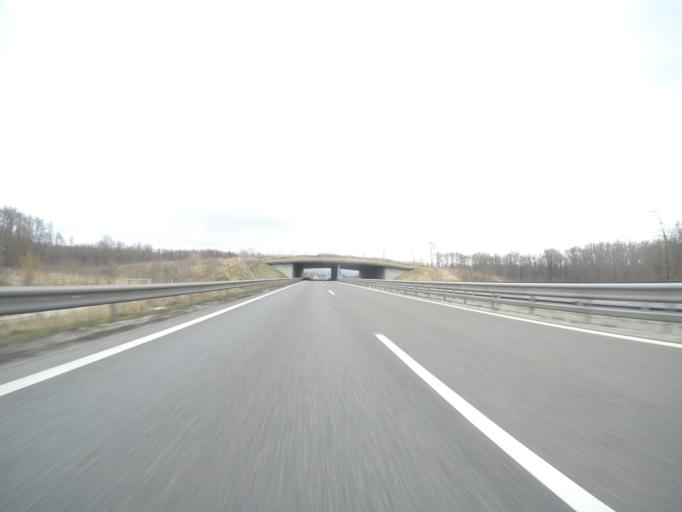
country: SI
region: Lendava-Lendva
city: Lendava
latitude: 46.5939
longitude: 16.4182
